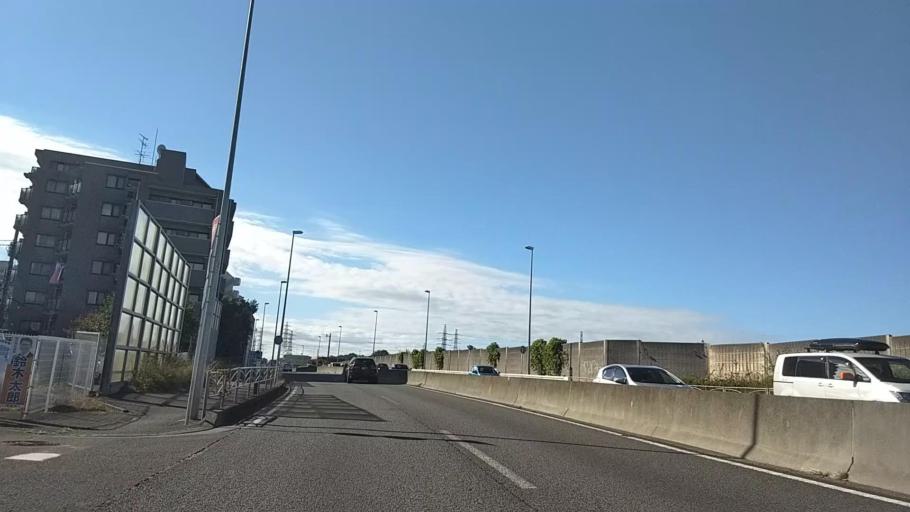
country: JP
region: Kanagawa
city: Fujisawa
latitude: 35.4066
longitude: 139.5287
